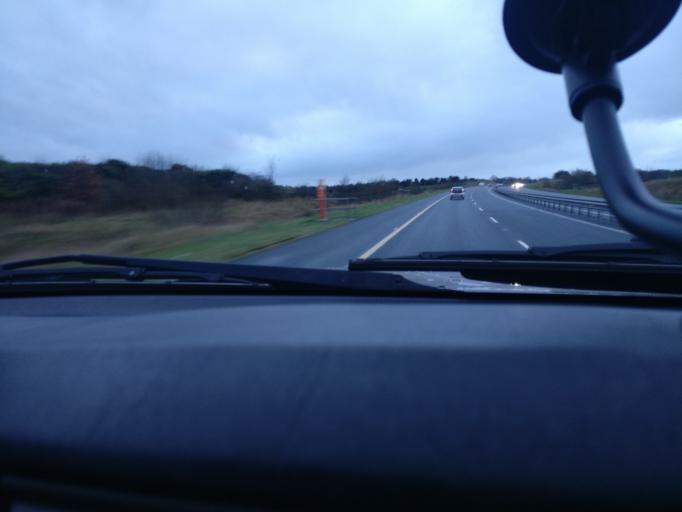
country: IE
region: Connaught
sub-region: County Galway
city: Ballinasloe
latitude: 53.3477
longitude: -8.0738
